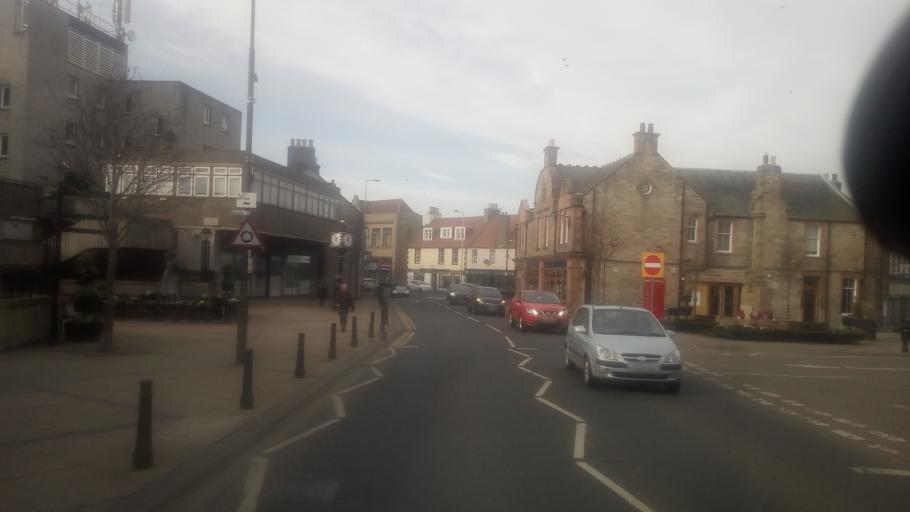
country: GB
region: Scotland
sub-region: East Lothian
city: Tranent
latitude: 55.9443
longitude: -2.9531
